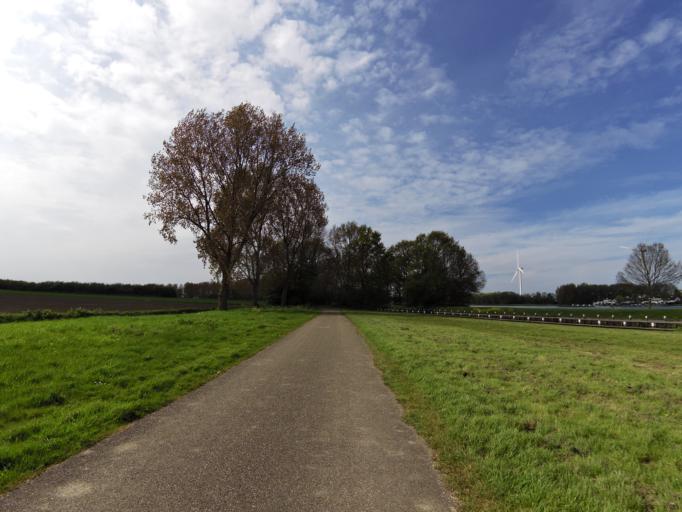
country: NL
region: South Holland
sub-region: Gemeente Brielle
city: Brielle
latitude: 51.9002
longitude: 4.2030
